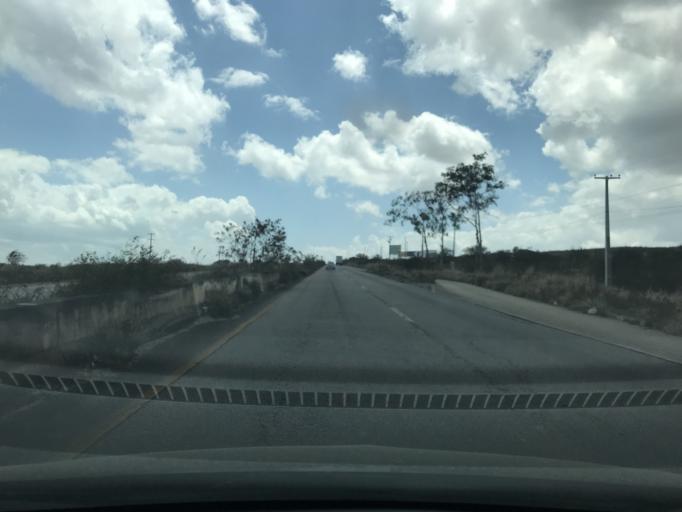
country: BR
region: Pernambuco
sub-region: Caruaru
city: Caruaru
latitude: -8.3039
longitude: -35.9269
